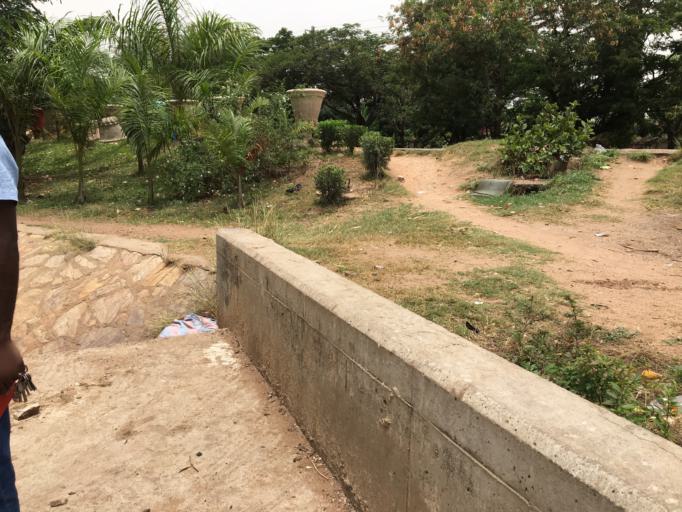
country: GH
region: Greater Accra
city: Accra
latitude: 5.5942
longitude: -0.1876
